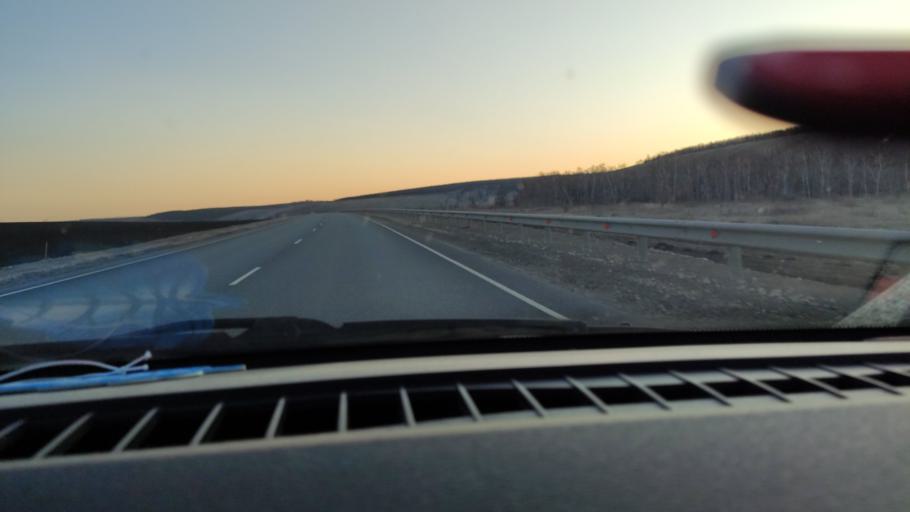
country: RU
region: Saratov
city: Yelshanka
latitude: 51.8592
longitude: 46.4972
